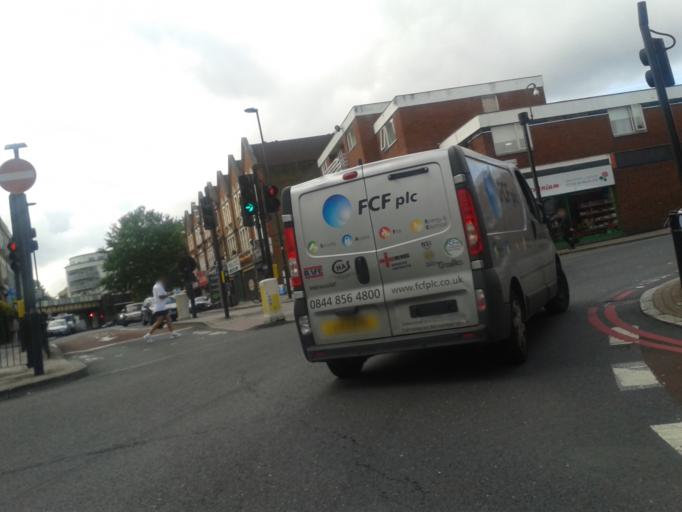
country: GB
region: England
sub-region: Greater London
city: Brixton Hill
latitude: 51.4404
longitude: -0.1062
